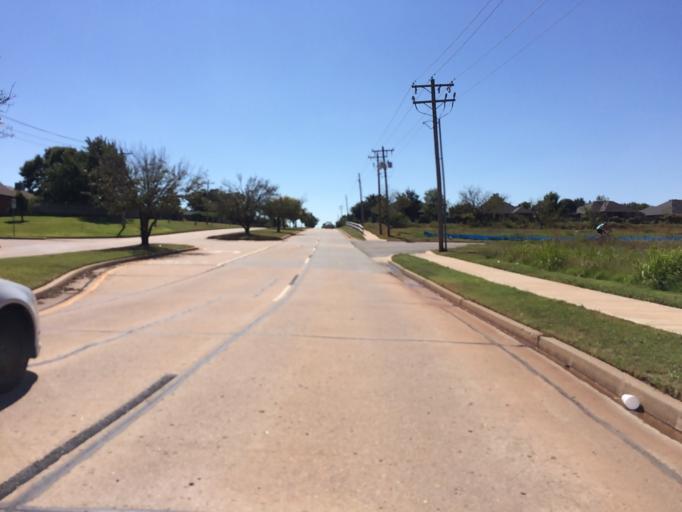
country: US
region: Oklahoma
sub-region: Cleveland County
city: Hall Park
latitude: 35.2454
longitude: -97.4061
